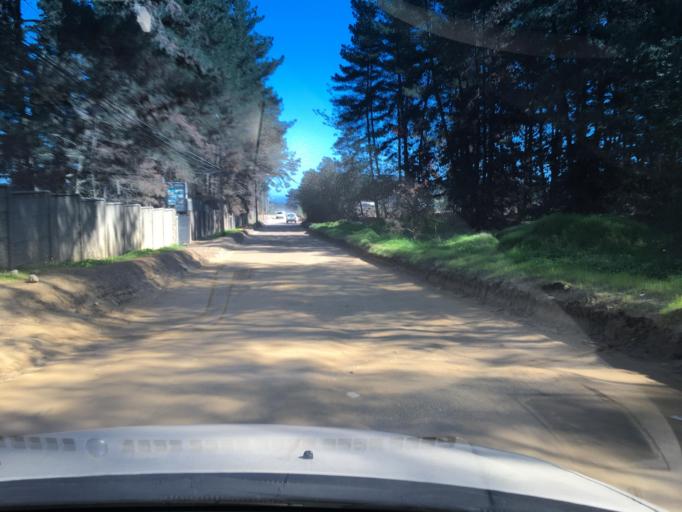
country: CL
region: Valparaiso
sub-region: Provincia de Valparaiso
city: Vina del Mar
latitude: -32.9567
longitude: -71.5232
